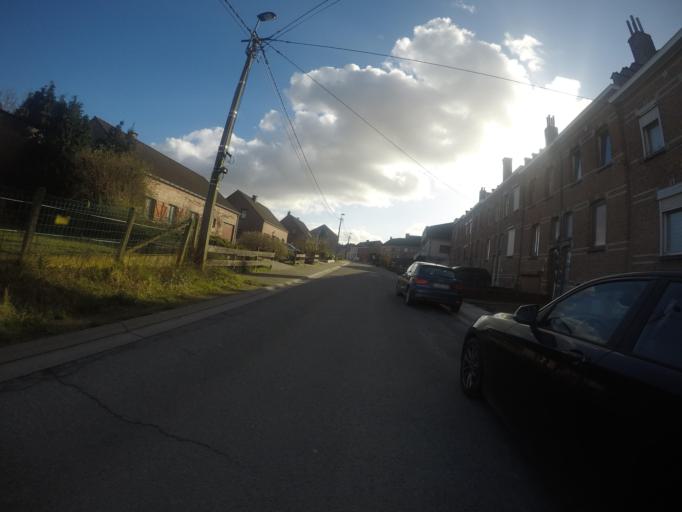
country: BE
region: Wallonia
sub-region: Province du Brabant Wallon
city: Tubize
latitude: 50.6794
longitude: 4.1560
